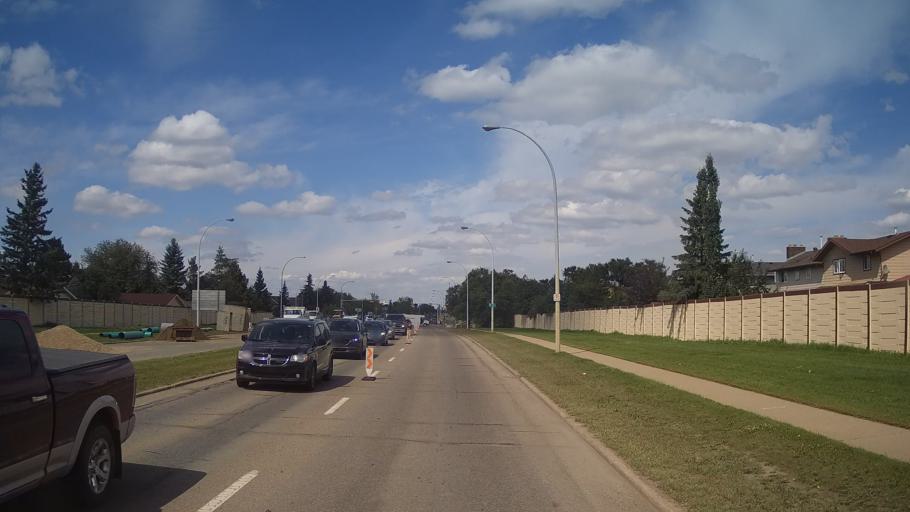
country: CA
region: Alberta
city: St. Albert
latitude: 53.5266
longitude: -113.6299
